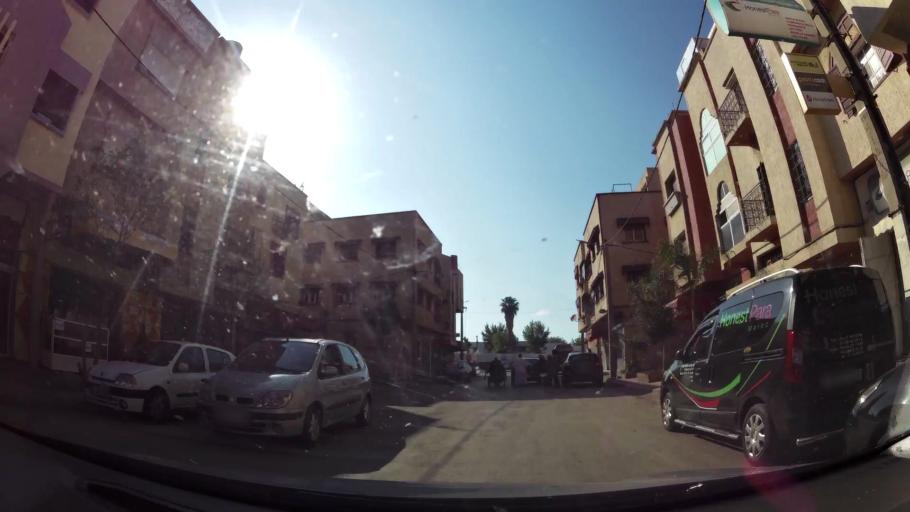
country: MA
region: Rabat-Sale-Zemmour-Zaer
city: Sale
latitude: 34.0445
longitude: -6.8153
